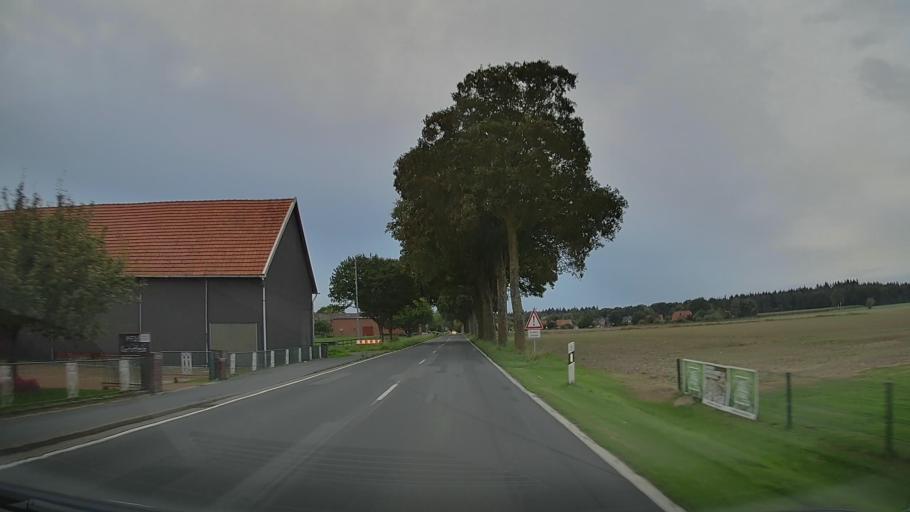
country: DE
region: Lower Saxony
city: Syke
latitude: 52.9061
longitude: 8.8743
